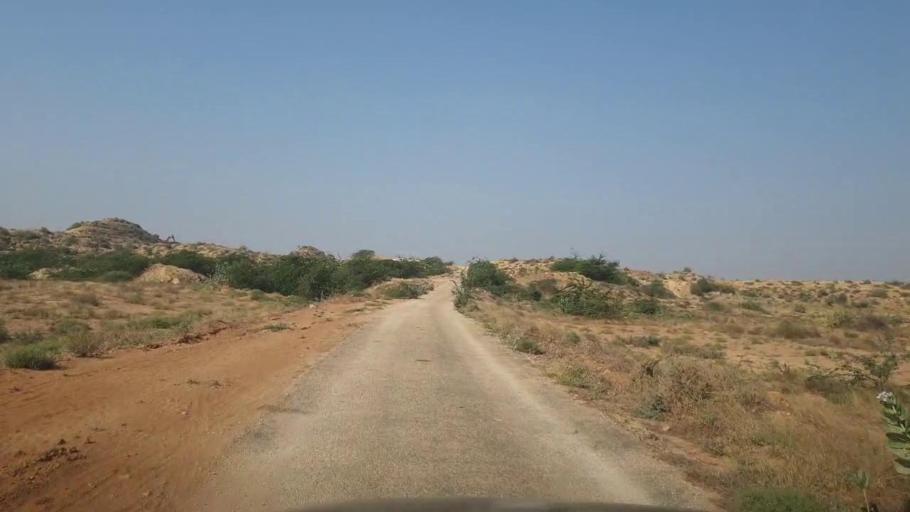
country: PK
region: Sindh
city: Gharo
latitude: 25.0472
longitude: 67.5494
